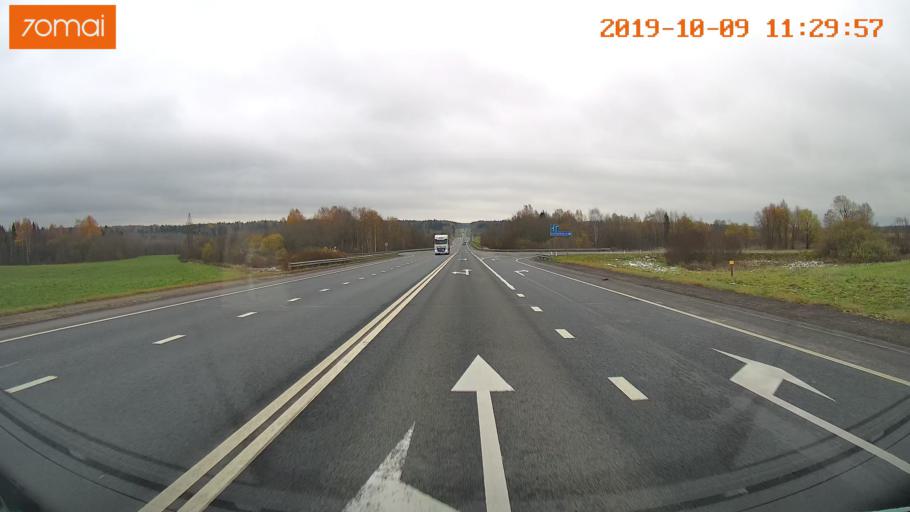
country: RU
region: Vologda
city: Vologda
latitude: 59.0580
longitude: 40.0645
